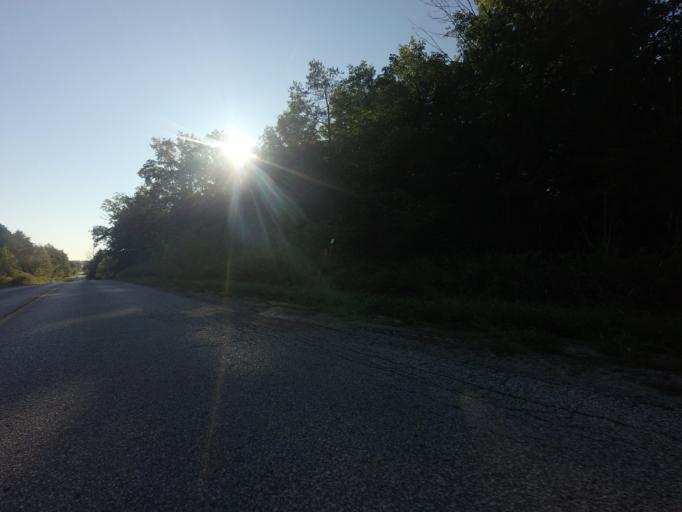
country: CA
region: Ontario
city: Bradford West Gwillimbury
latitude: 44.0433
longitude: -79.7685
